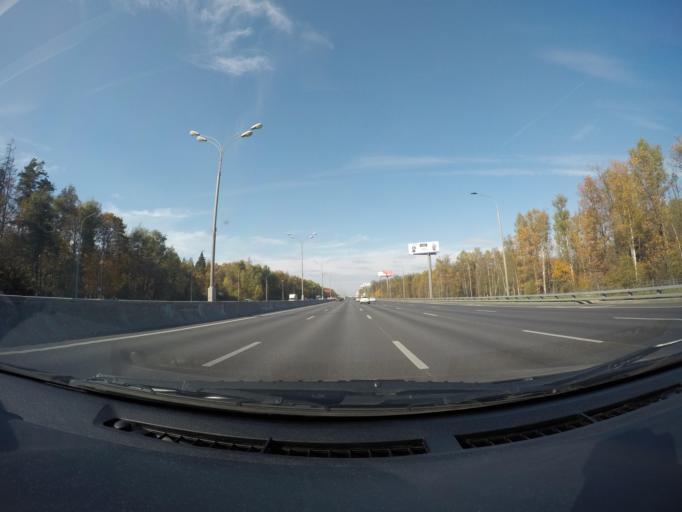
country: RU
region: Moscow
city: Gol'yanovo
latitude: 55.8532
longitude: 37.7830
